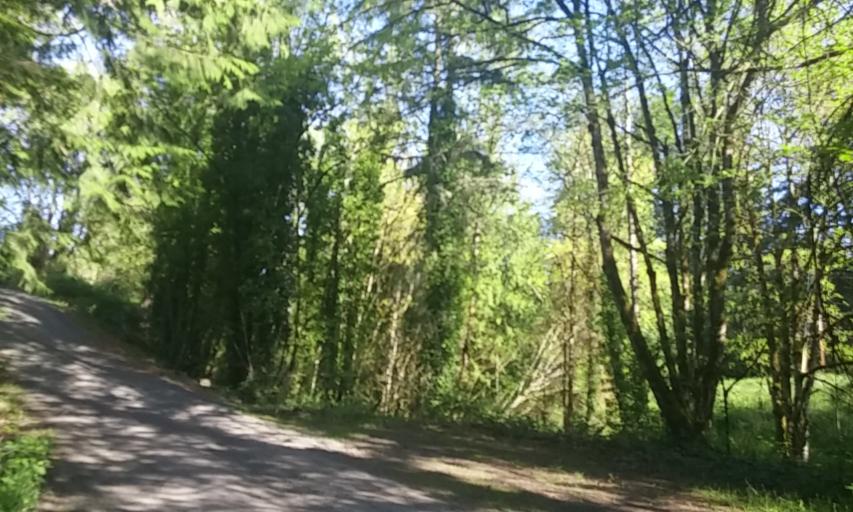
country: US
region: Oregon
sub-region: Washington County
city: Cedar Mill
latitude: 45.5493
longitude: -122.7929
